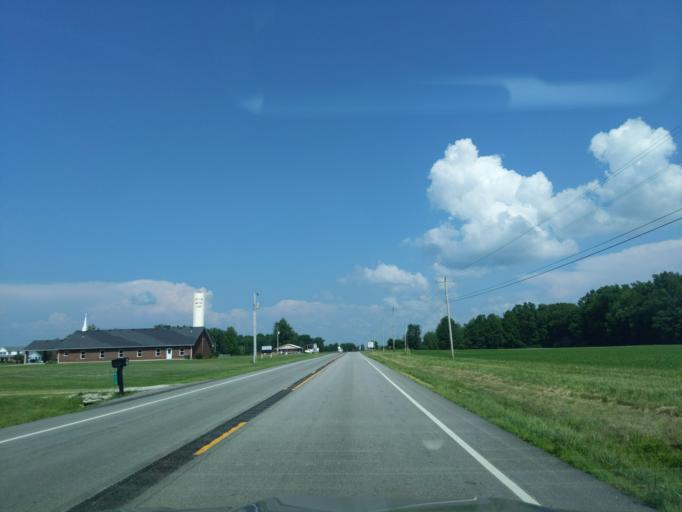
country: US
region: Indiana
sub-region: Ripley County
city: Osgood
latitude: 39.0751
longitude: -85.3513
